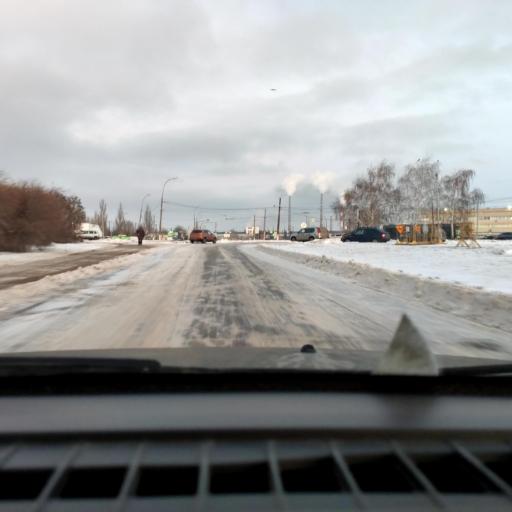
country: RU
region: Samara
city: Tol'yatti
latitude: 53.5516
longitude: 49.2629
